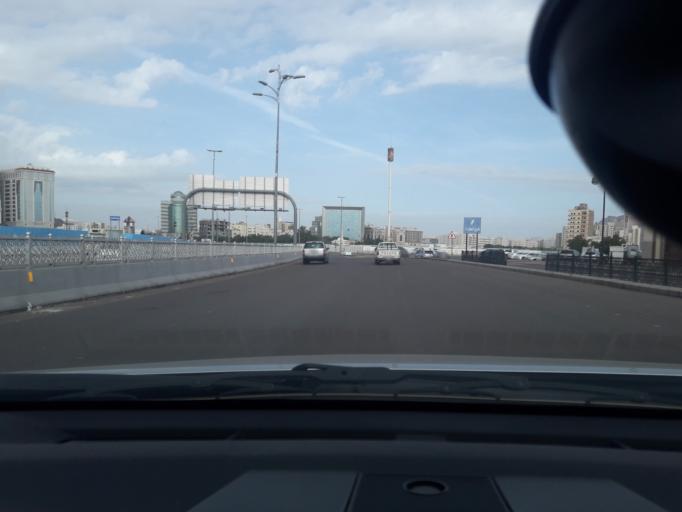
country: SA
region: Al Madinah al Munawwarah
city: Medina
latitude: 24.4716
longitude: 39.6183
